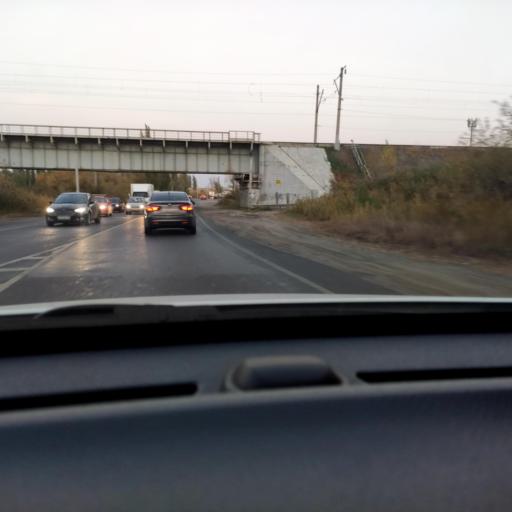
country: RU
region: Voronezj
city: Maslovka
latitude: 51.6224
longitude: 39.2568
